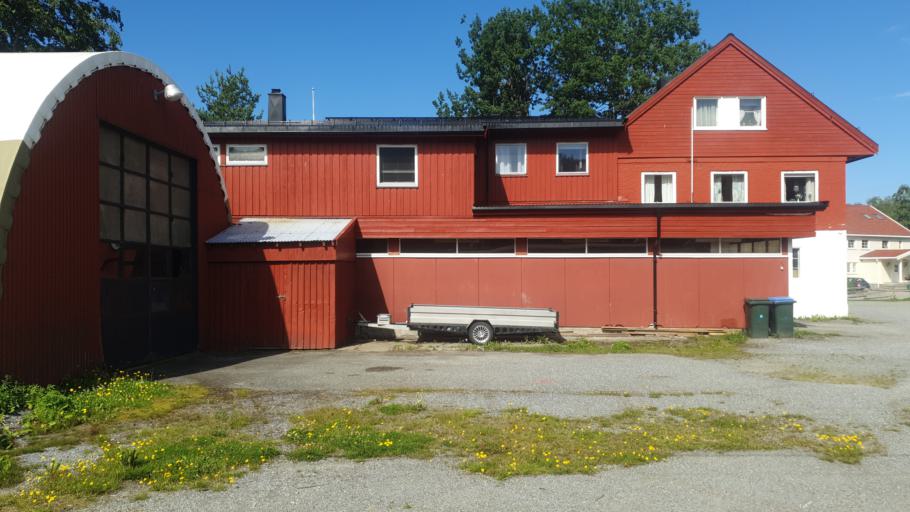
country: NO
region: Sor-Trondelag
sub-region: Orkdal
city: Orkanger
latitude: 63.2845
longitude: 9.8388
